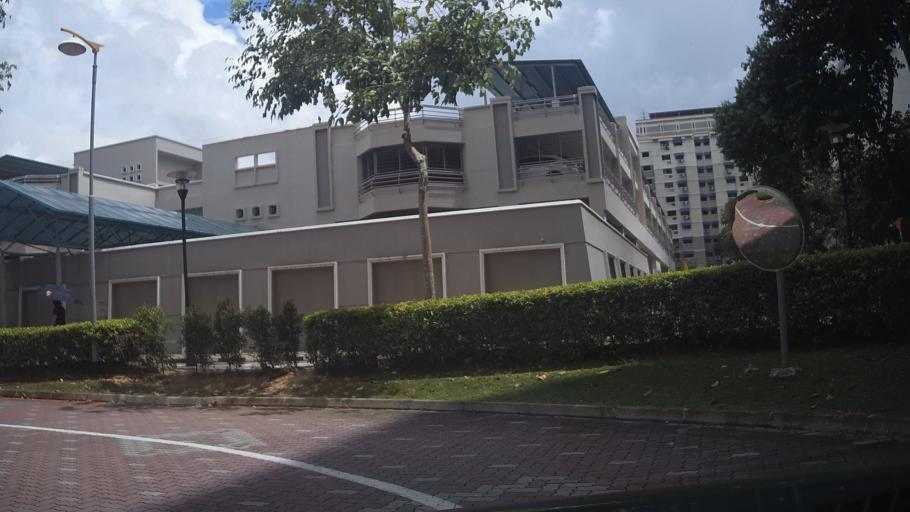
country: MY
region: Johor
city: Johor Bahru
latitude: 1.4454
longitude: 103.7973
